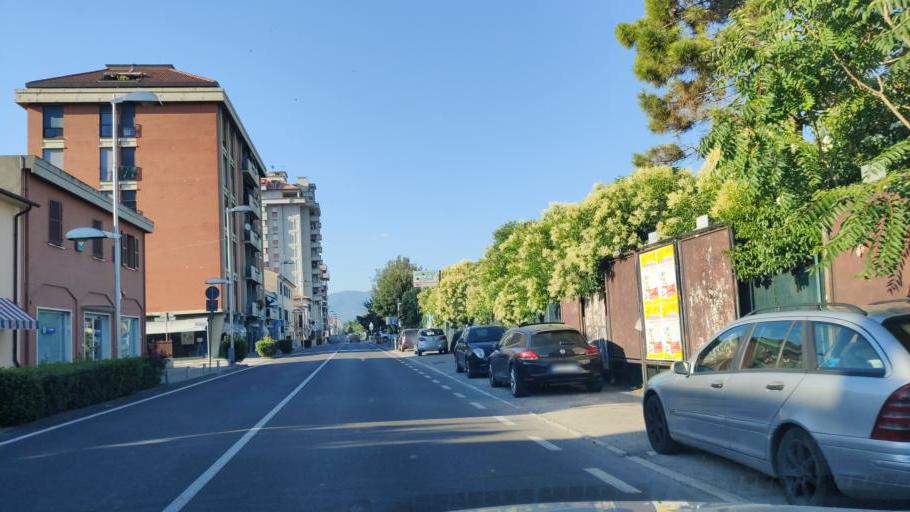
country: IT
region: Umbria
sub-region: Provincia di Terni
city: Narni Scalo
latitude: 42.5335
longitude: 12.5186
